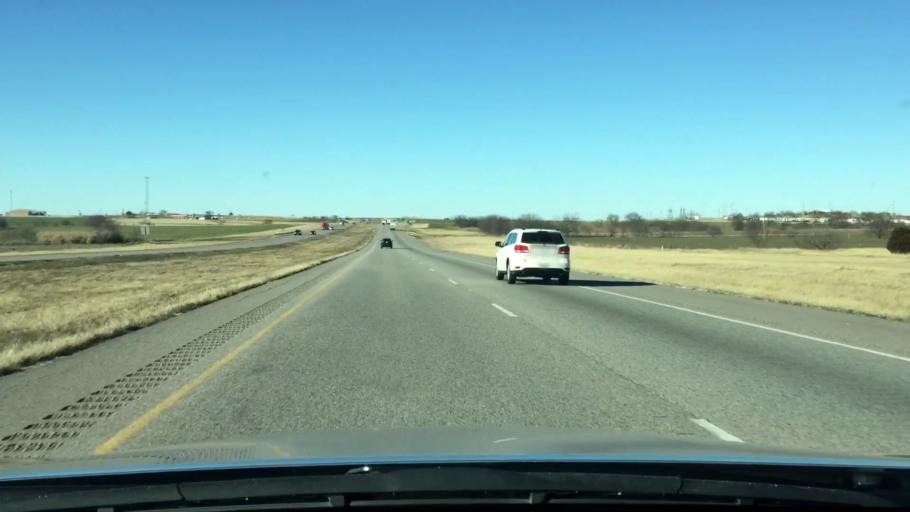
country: US
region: Texas
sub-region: Hill County
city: Itasca
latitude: 32.1438
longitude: -97.1232
